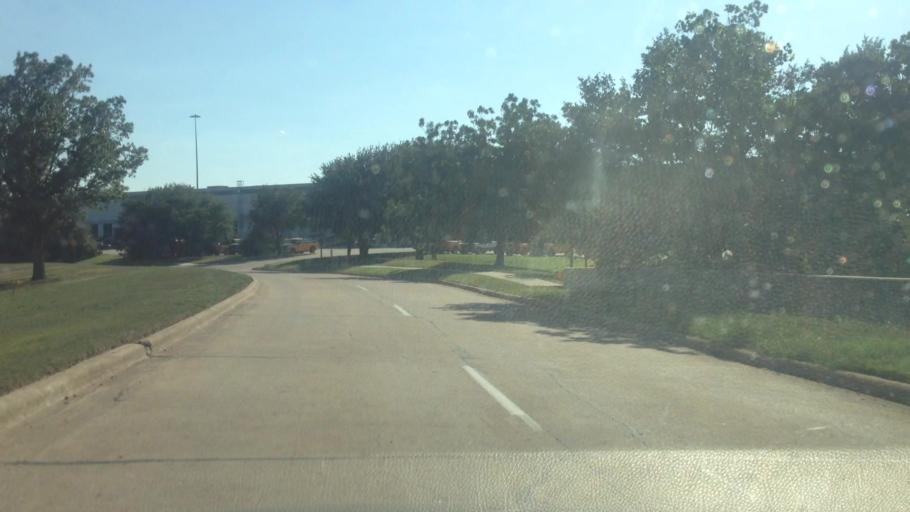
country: US
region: Texas
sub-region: Dallas County
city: Irving
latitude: 32.8405
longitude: -96.9199
